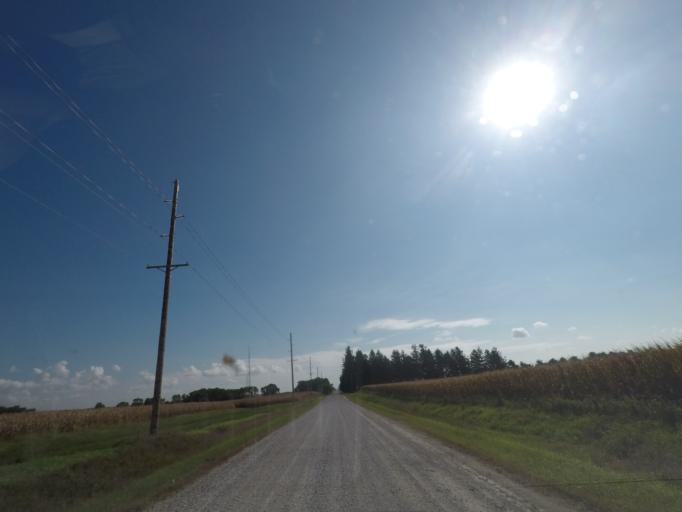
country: US
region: Iowa
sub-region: Story County
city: Nevada
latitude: 42.0344
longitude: -93.3987
